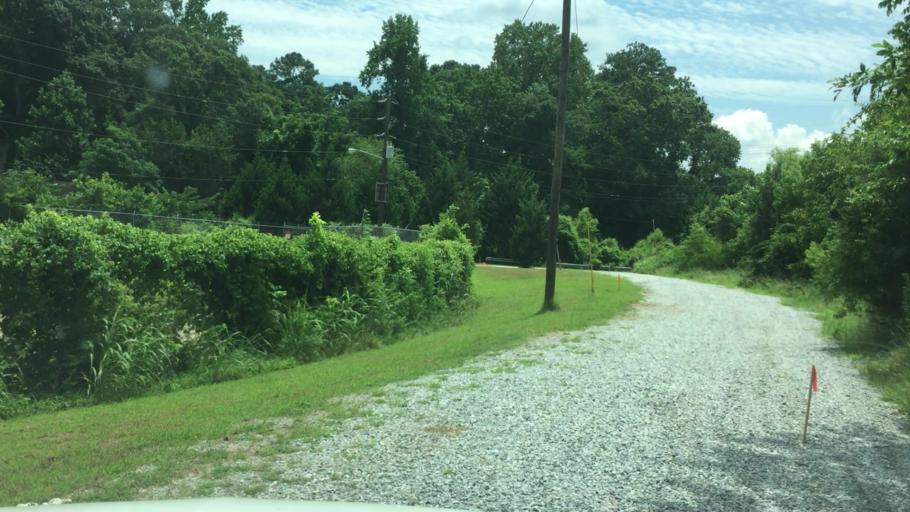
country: US
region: Georgia
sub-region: Fulton County
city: Atlanta
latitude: 33.7188
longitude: -84.3608
